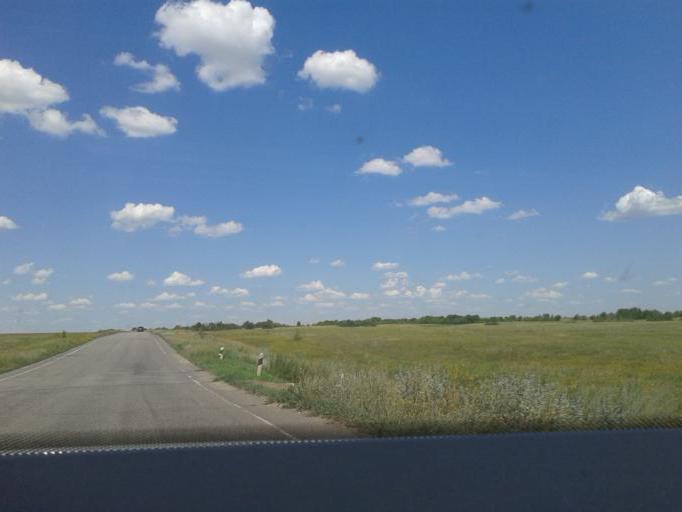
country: RU
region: Volgograd
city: Frolovo
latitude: 49.6770
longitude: 43.6346
